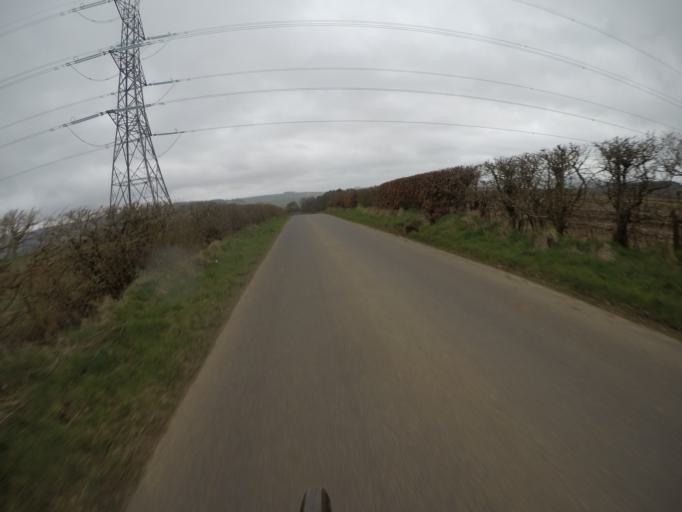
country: GB
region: Scotland
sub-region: East Ayrshire
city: Newmilns
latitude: 55.6184
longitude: -4.3435
